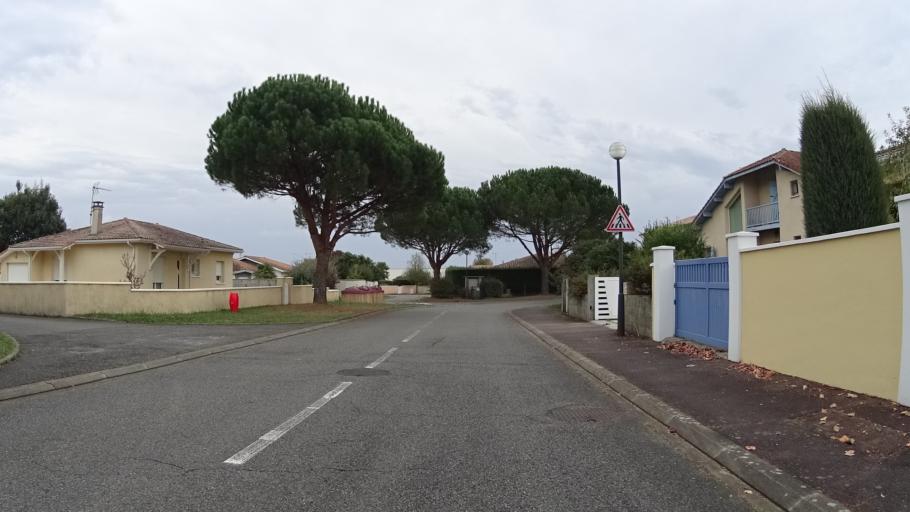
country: FR
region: Aquitaine
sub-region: Departement des Landes
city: Saint-Paul-les-Dax
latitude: 43.7290
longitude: -1.0782
